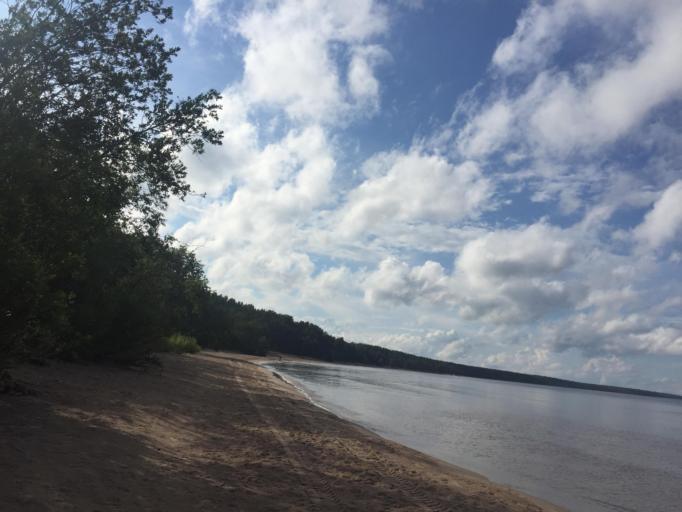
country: RU
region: Leningrad
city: Priozersk
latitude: 60.9739
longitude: 30.2991
